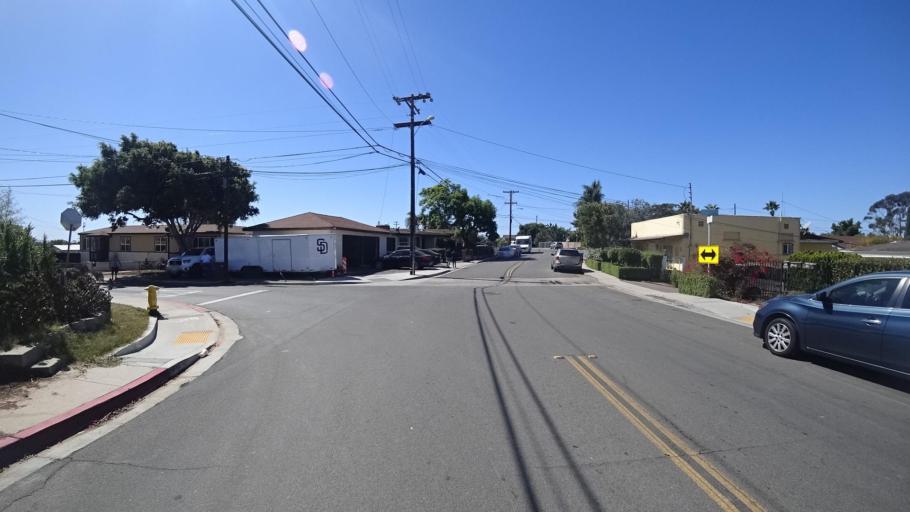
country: US
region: California
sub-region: San Diego County
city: National City
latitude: 32.6654
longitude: -117.0812
